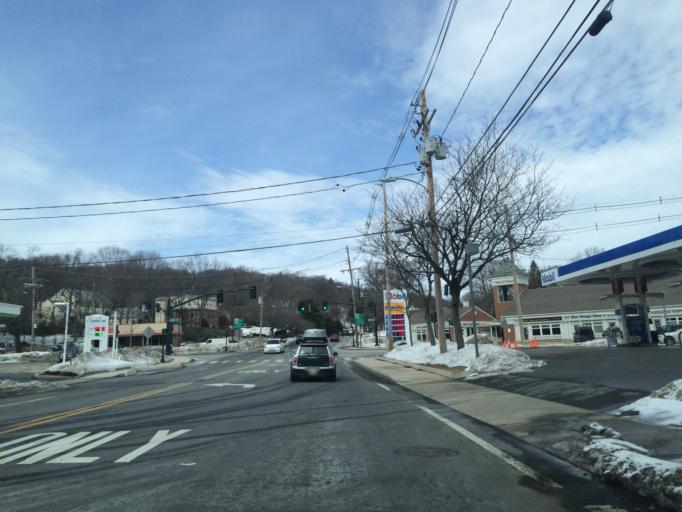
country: US
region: Massachusetts
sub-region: Middlesex County
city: Lexington
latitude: 42.4352
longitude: -71.2344
